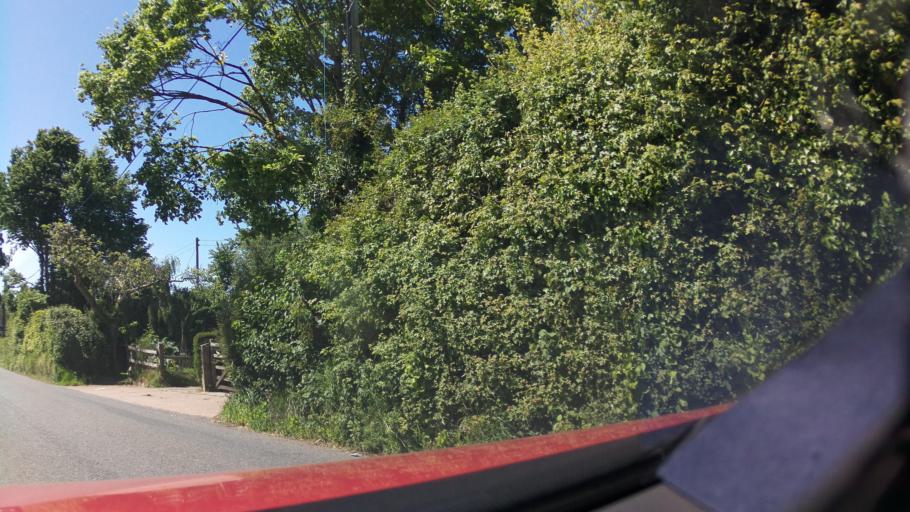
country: GB
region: England
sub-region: Devon
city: Ottery St Mary
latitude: 50.7782
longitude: -3.2540
